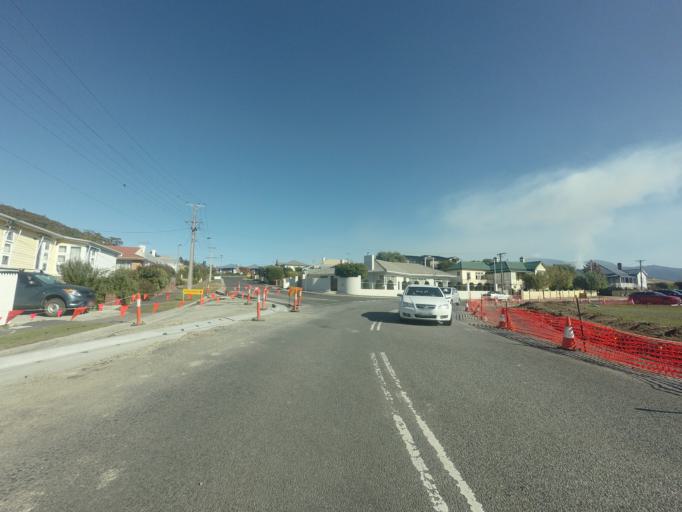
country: AU
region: Tasmania
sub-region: Clarence
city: Lindisfarne
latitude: -42.8499
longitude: 147.3607
